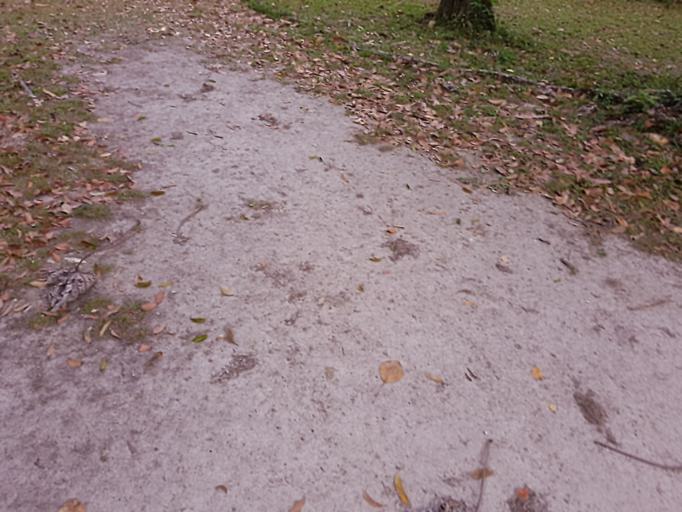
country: GT
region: Peten
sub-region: Municipio de San Jose
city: San Jose
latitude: 17.2253
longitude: -89.6193
